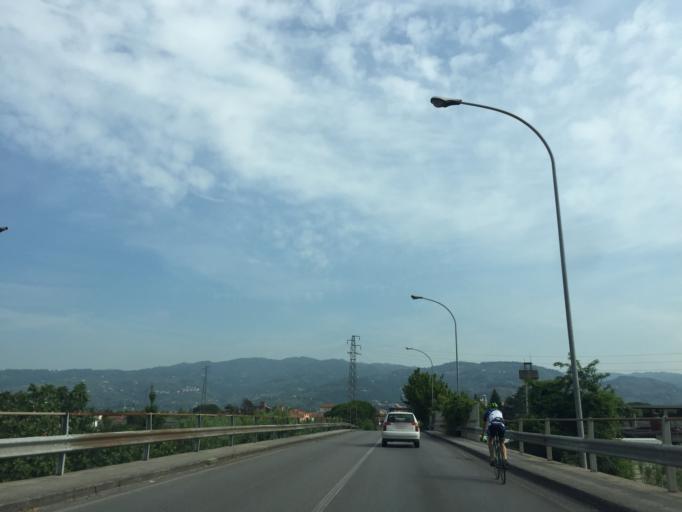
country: IT
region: Tuscany
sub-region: Provincia di Pistoia
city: Montecatini-Terme
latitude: 43.8695
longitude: 10.7679
